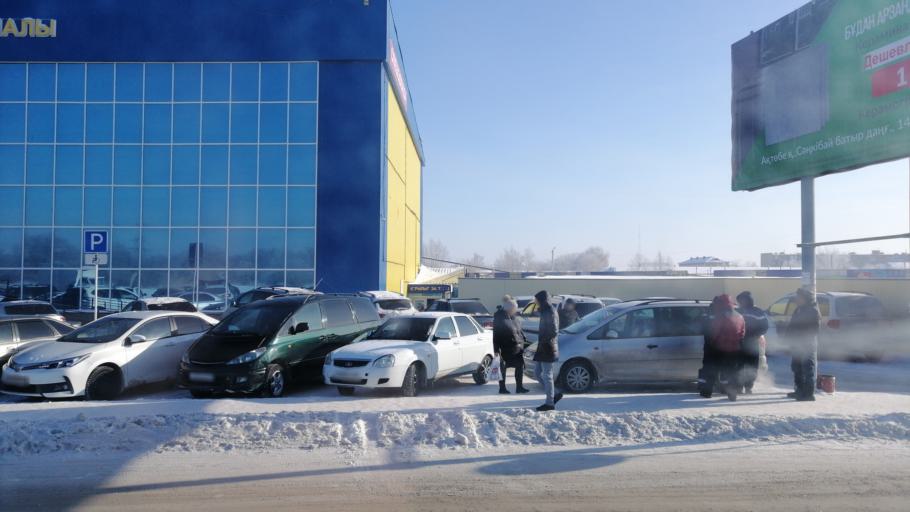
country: KZ
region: Aqtoebe
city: Aqtobe
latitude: 50.2949
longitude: 57.1978
